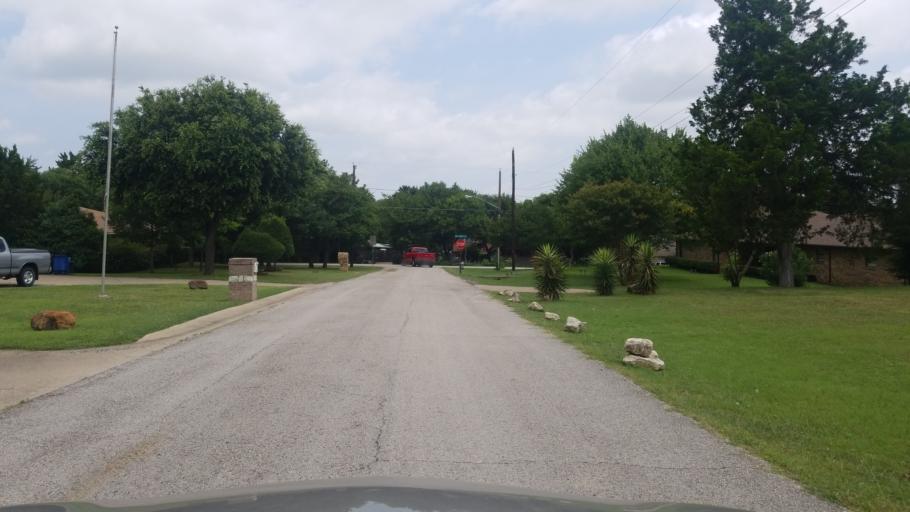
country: US
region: Texas
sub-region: Dallas County
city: Duncanville
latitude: 32.6839
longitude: -96.9328
